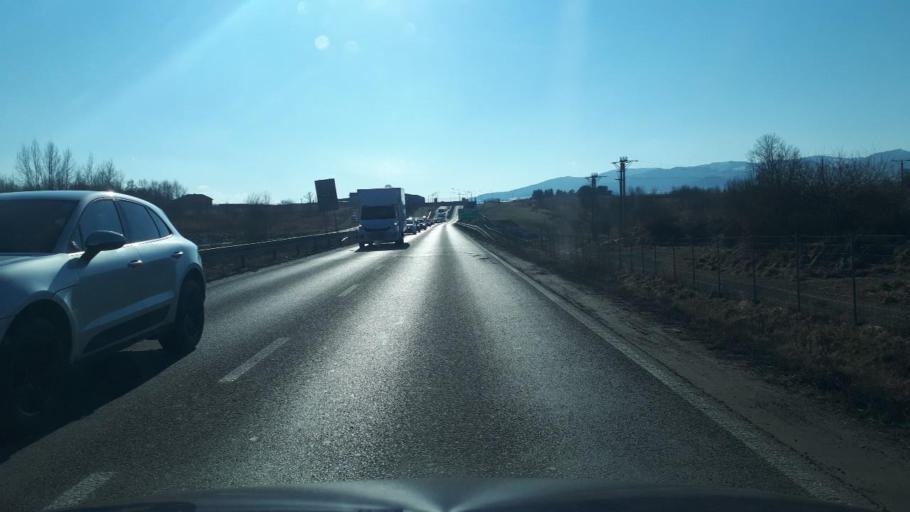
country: PL
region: Silesian Voivodeship
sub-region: Powiat zywiecki
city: Pietrzykowice
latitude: 49.6872
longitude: 19.1745
